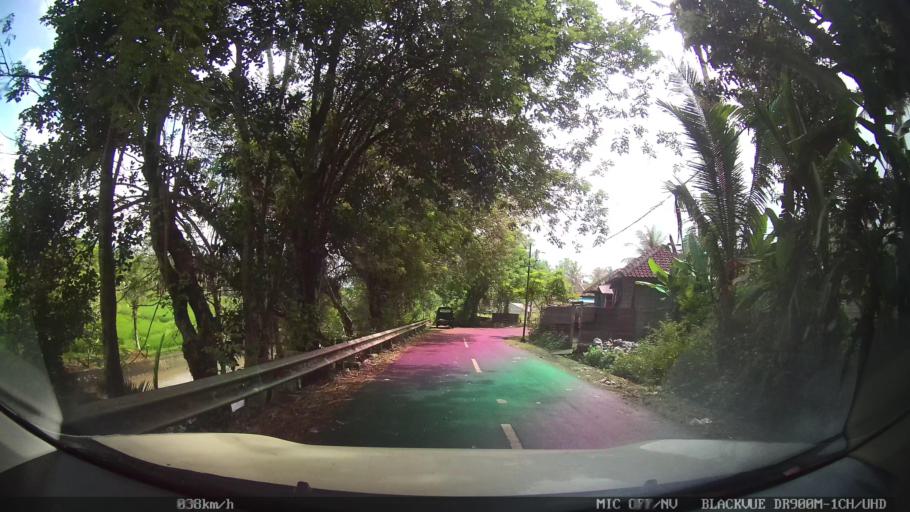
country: ID
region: Bali
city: Banjar Parekan
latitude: -8.5689
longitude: 115.2030
